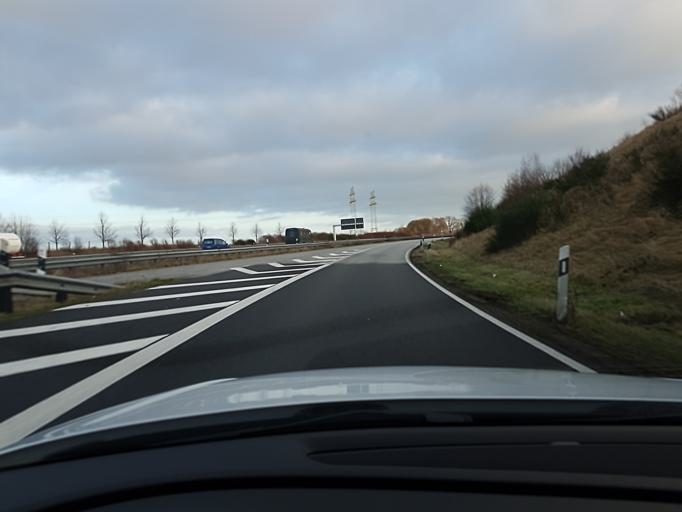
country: DE
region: Schleswig-Holstein
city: Hamberge
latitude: 53.8484
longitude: 10.5977
